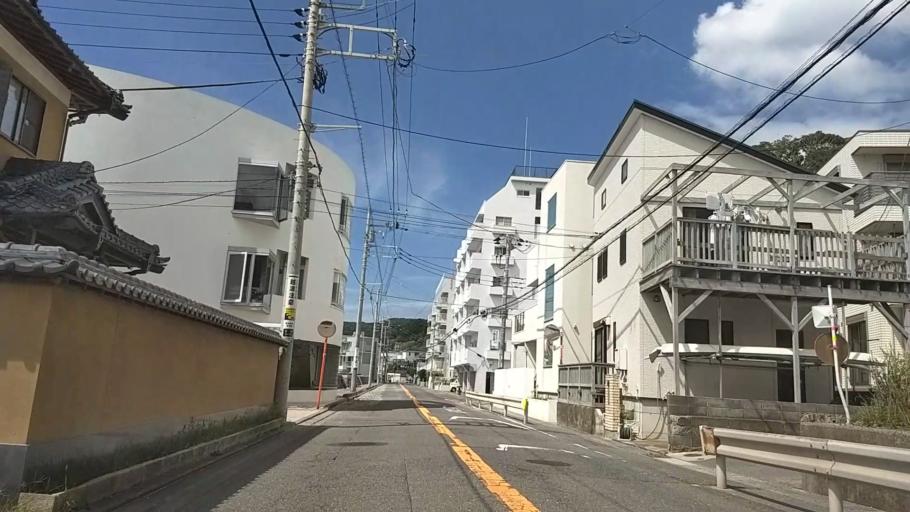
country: JP
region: Kanagawa
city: Hayama
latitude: 35.2256
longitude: 139.6038
